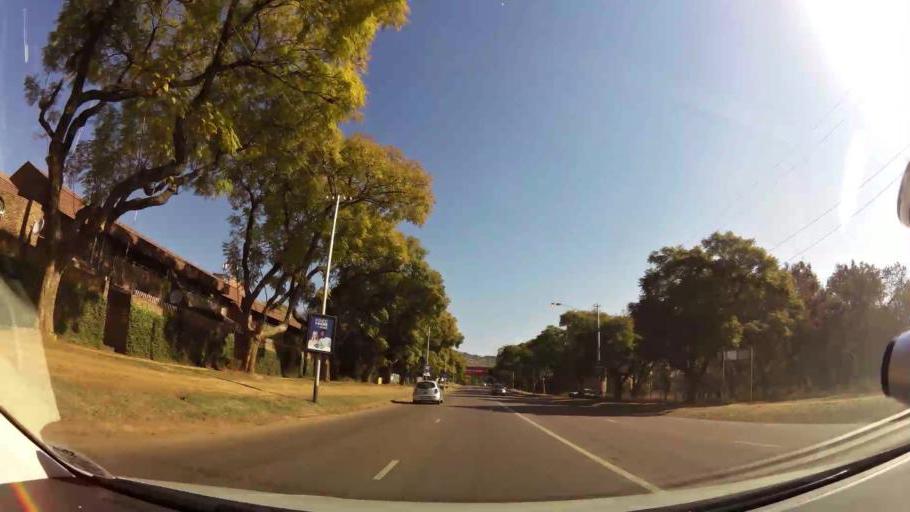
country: ZA
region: Gauteng
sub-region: City of Tshwane Metropolitan Municipality
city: Pretoria
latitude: -25.7726
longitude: 28.2279
